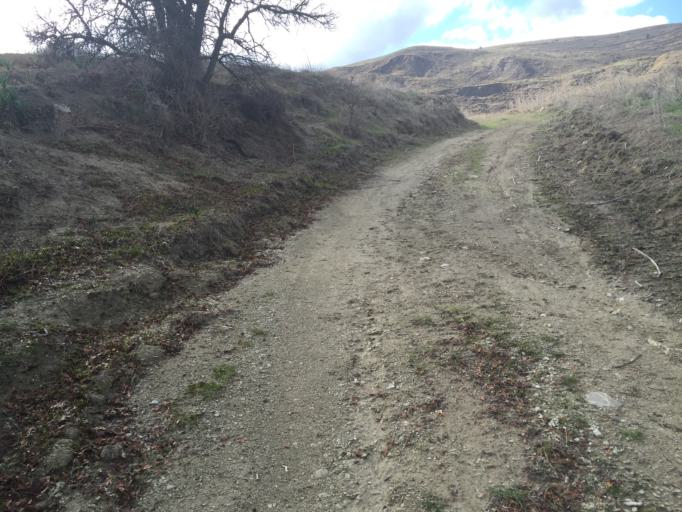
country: CY
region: Limassol
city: Pachna
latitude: 34.8717
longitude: 32.6623
